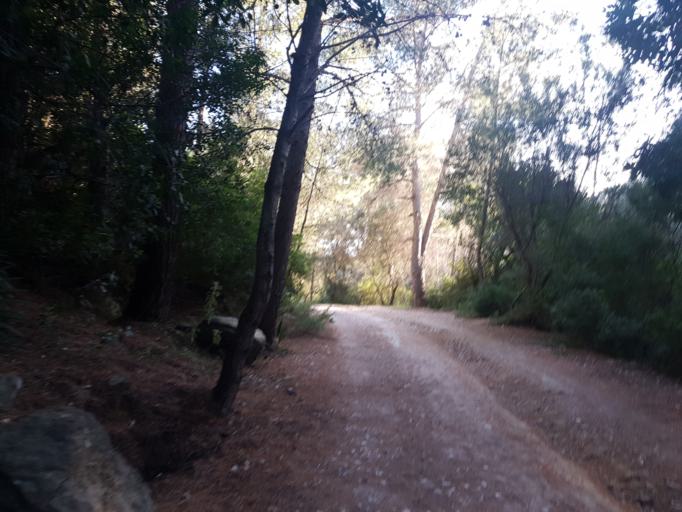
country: ES
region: Andalusia
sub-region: Provincia de Malaga
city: Marbella
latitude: 36.5384
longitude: -4.8839
